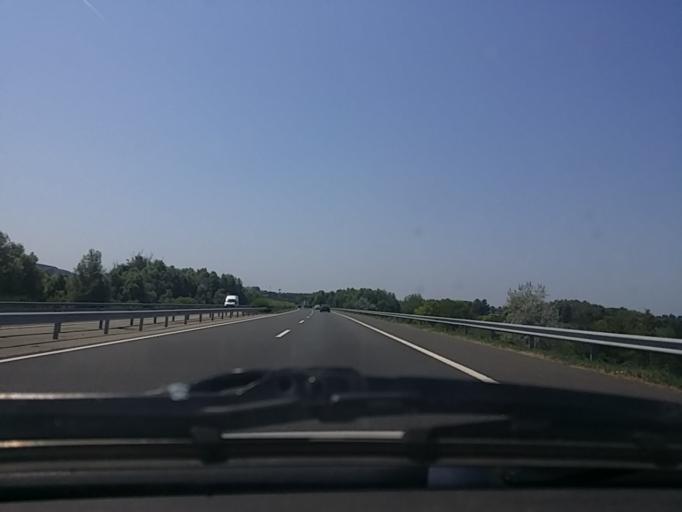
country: HU
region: Somogy
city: Balatonlelle
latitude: 46.7838
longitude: 17.7303
